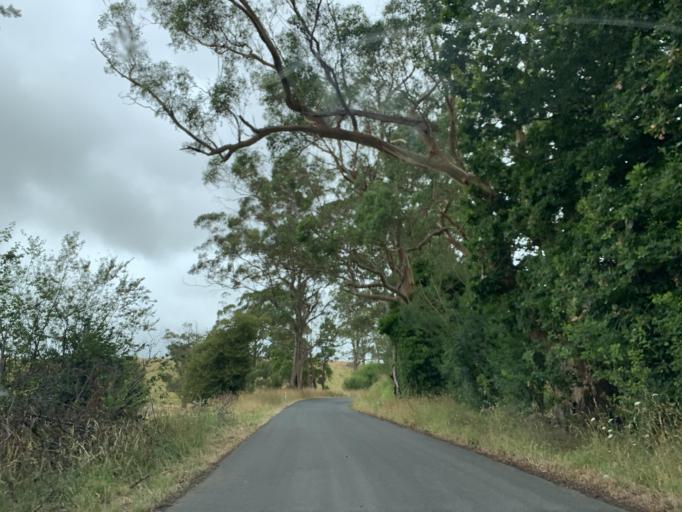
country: AU
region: Victoria
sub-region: Baw Baw
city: Warragul
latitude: -38.2948
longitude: 145.8488
